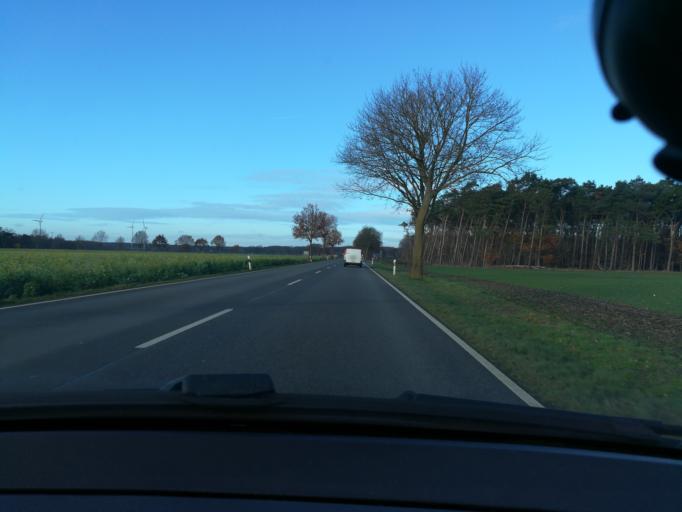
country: DE
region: Lower Saxony
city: Kirchdorf
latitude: 52.5528
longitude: 8.8601
